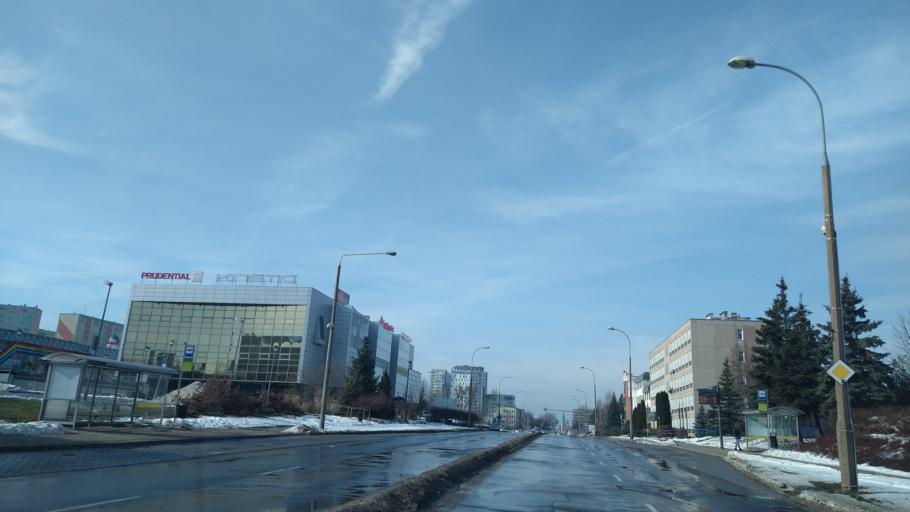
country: PL
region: Warmian-Masurian Voivodeship
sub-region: Powiat olsztynski
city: Olsztyn
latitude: 53.7732
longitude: 20.4999
